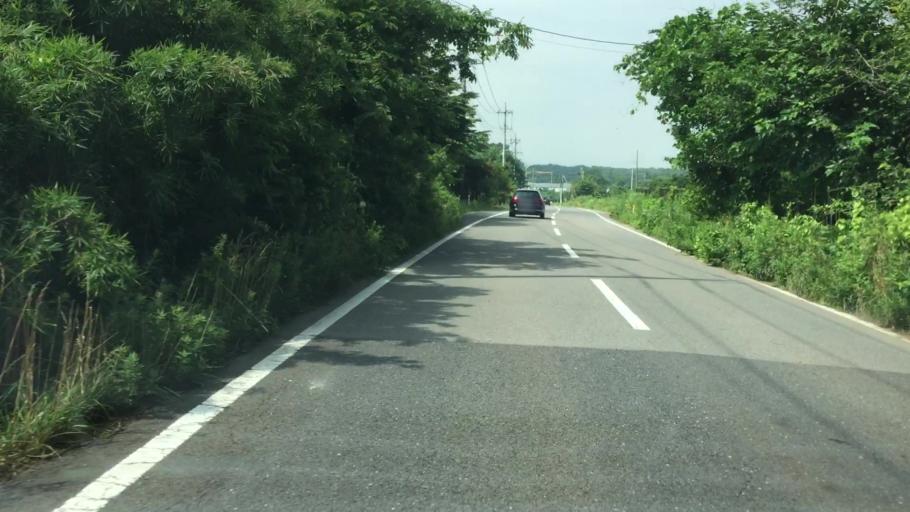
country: JP
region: Tochigi
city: Kuroiso
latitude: 37.0832
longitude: 140.0551
